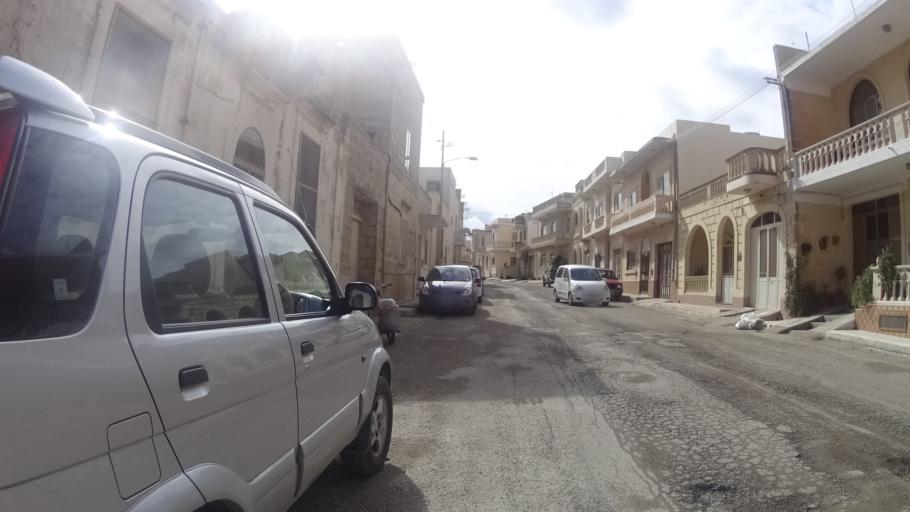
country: MT
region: In-Nadur
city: Nadur
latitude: 36.0446
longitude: 14.2988
